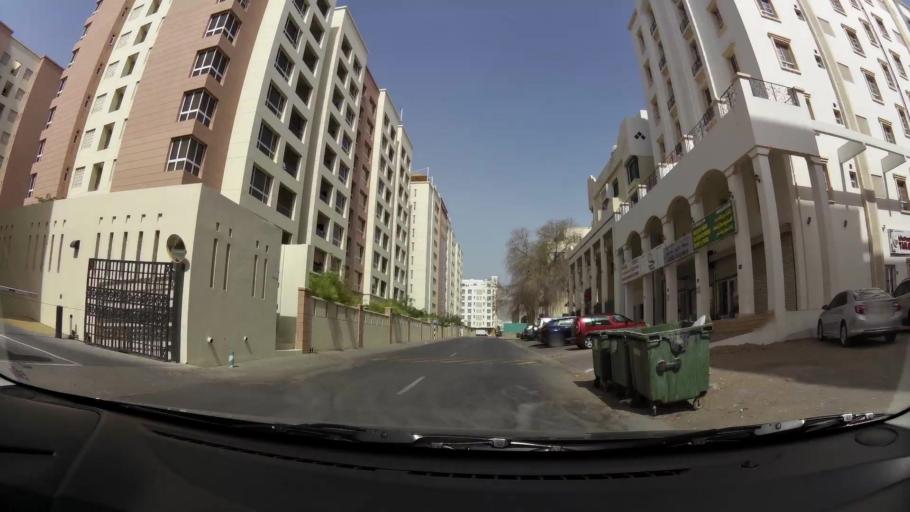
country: OM
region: Muhafazat Masqat
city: Bawshar
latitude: 23.5810
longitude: 58.3969
